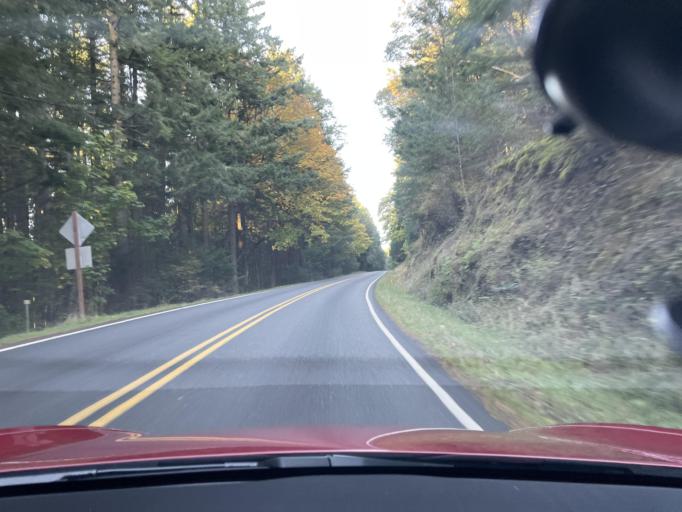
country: US
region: Washington
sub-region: San Juan County
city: Friday Harbor
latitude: 48.5855
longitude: -123.1435
